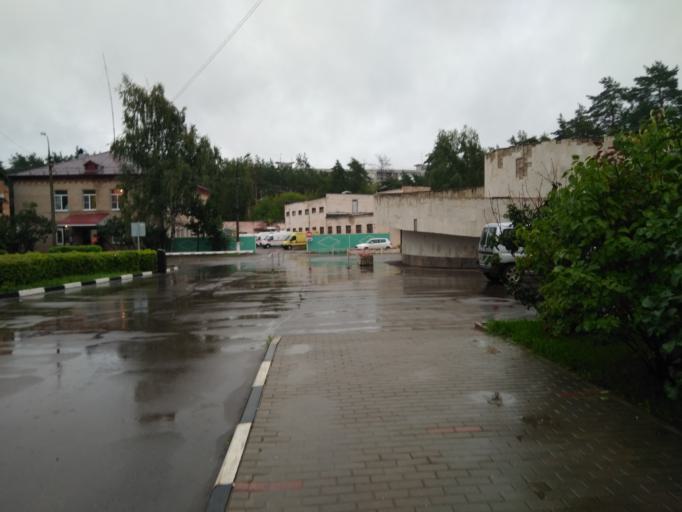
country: RU
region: Moskovskaya
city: Zhukovskiy
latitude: 55.5985
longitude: 38.1281
